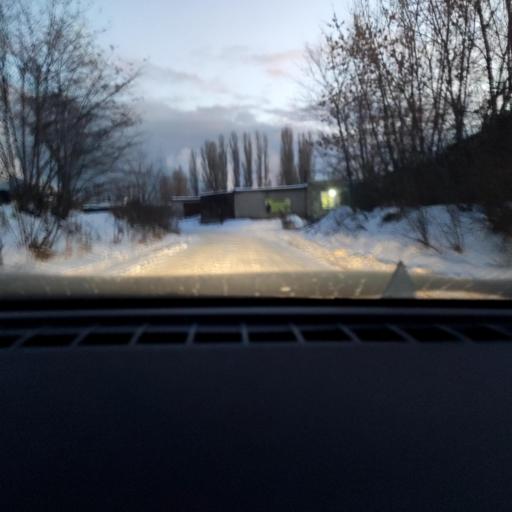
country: RU
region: Voronezj
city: Voronezh
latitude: 51.6219
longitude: 39.2308
